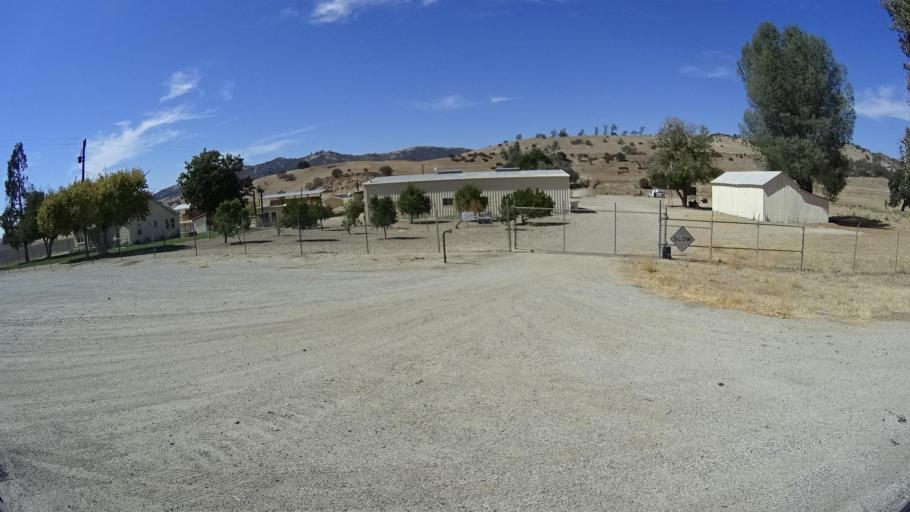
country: US
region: California
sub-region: San Luis Obispo County
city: San Miguel
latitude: 35.9560
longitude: -120.6543
